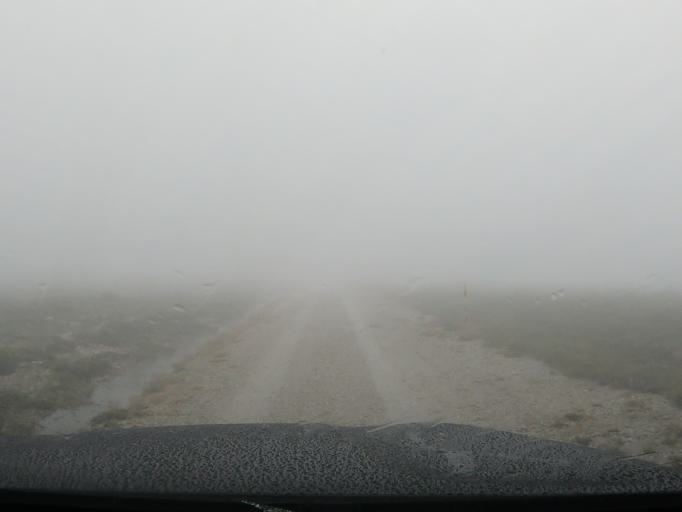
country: PT
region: Vila Real
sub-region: Vila Real
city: Vila Real
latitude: 41.3441
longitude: -7.8418
